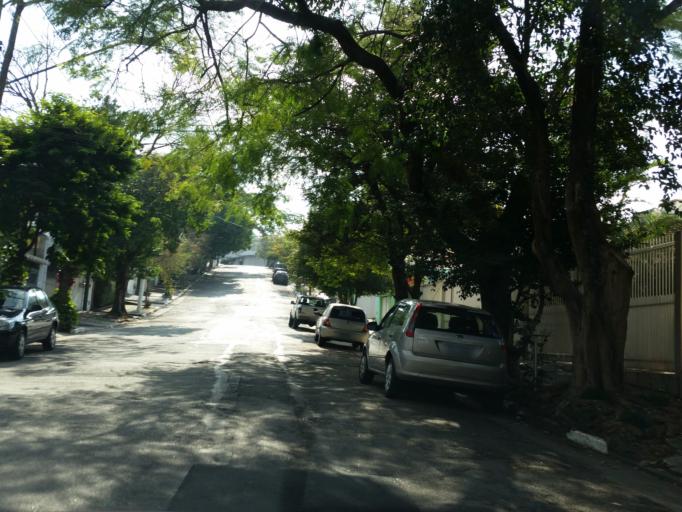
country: BR
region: Sao Paulo
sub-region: Diadema
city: Diadema
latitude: -23.6525
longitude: -46.6986
